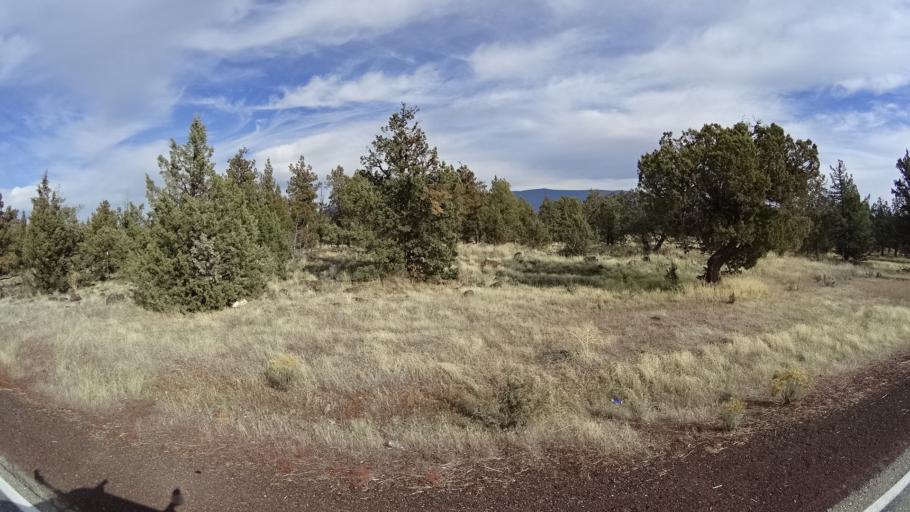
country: US
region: California
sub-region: Siskiyou County
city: Montague
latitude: 41.6089
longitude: -122.3993
